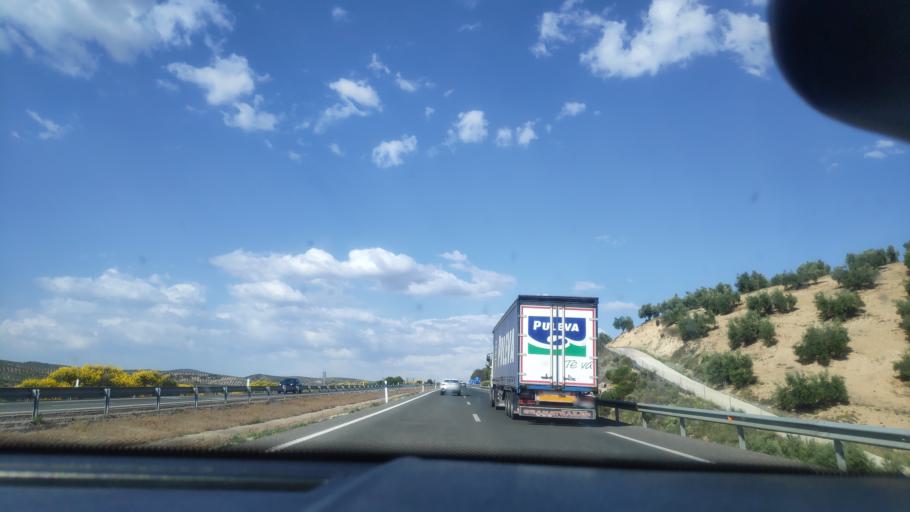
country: ES
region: Andalusia
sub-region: Provincia de Granada
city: Campotejar
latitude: 37.4873
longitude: -3.5961
